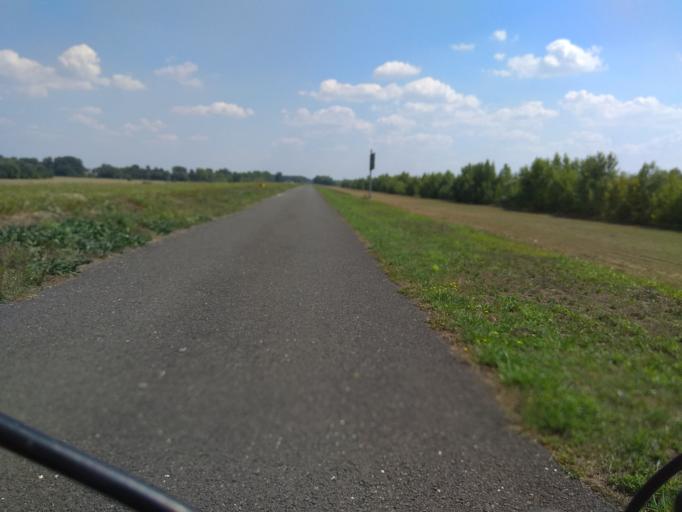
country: SK
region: Trnavsky
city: Gabcikovo
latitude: 47.8307
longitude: 17.6009
